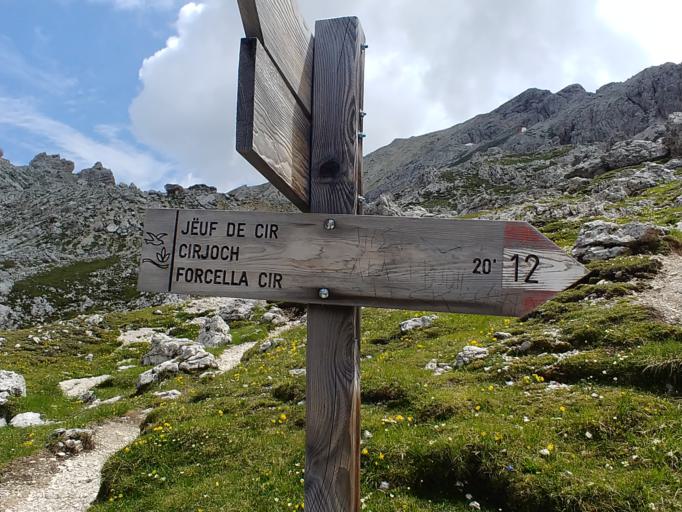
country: IT
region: Trentino-Alto Adige
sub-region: Bolzano
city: Selva
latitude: 46.5630
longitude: 11.8160
